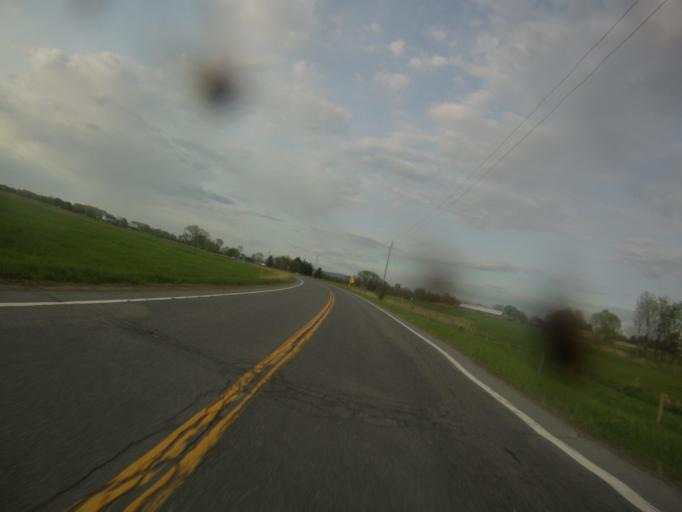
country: US
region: New York
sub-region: Essex County
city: Port Henry
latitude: 43.9994
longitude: -73.4222
